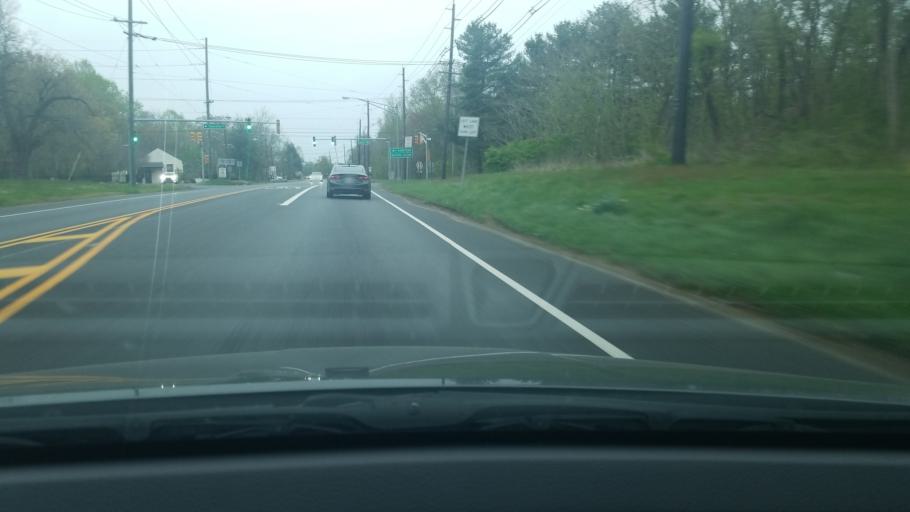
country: US
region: New Jersey
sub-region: Burlington County
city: Medford Lakes
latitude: 39.8992
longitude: -74.7901
